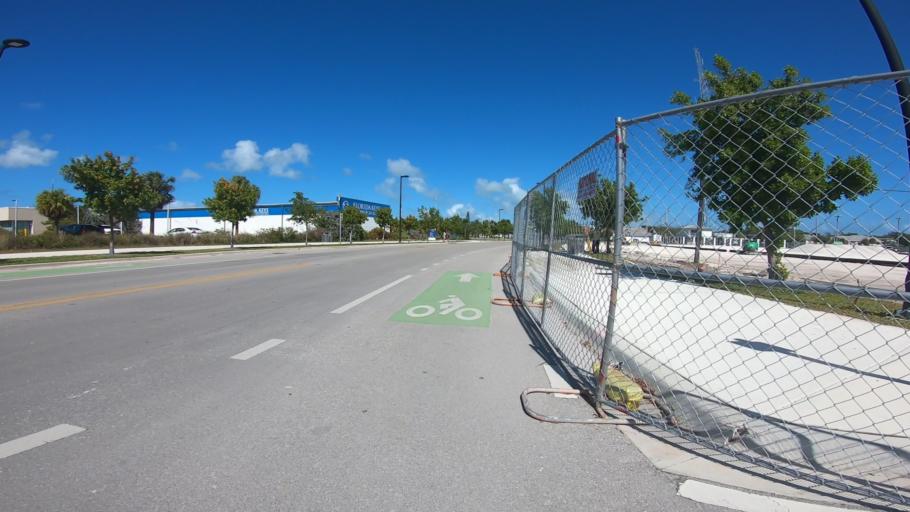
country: US
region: Florida
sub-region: Monroe County
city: Key West
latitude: 24.5507
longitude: -81.8078
